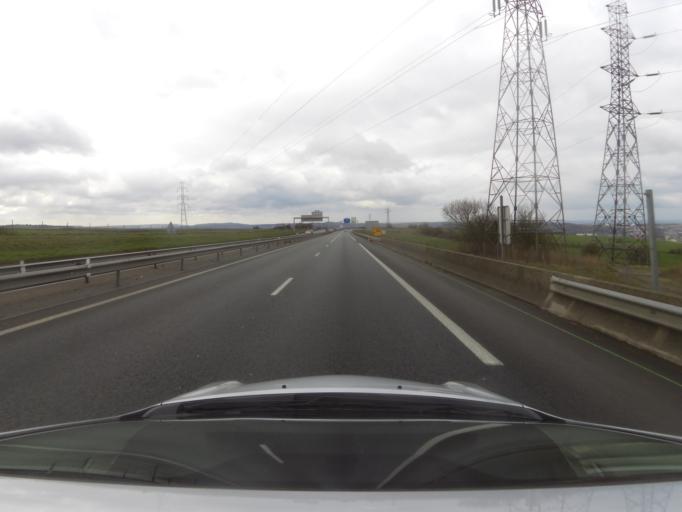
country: FR
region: Nord-Pas-de-Calais
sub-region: Departement du Pas-de-Calais
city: Boulogne-sur-Mer
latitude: 50.7126
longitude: 1.6429
